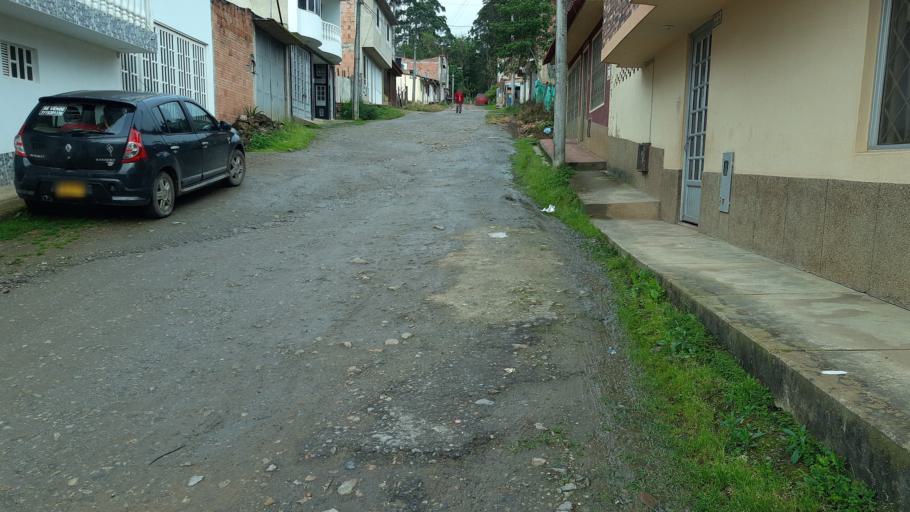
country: CO
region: Boyaca
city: Garagoa
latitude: 5.0865
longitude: -73.3609
